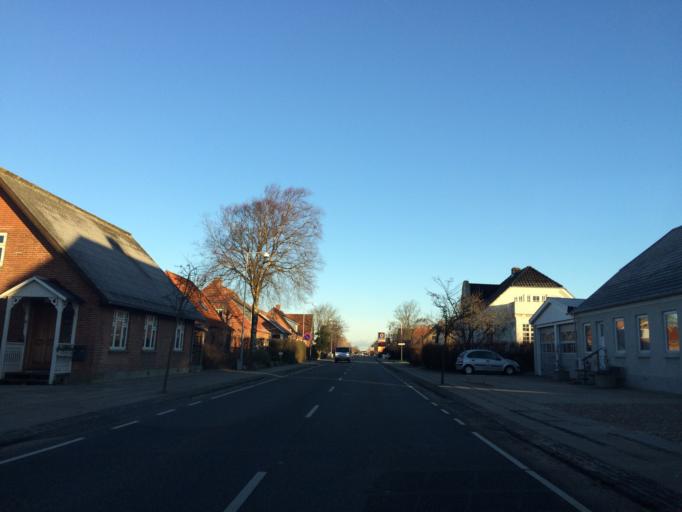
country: DK
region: Central Jutland
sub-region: Lemvig Kommune
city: Lemvig
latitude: 56.4148
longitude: 8.3080
